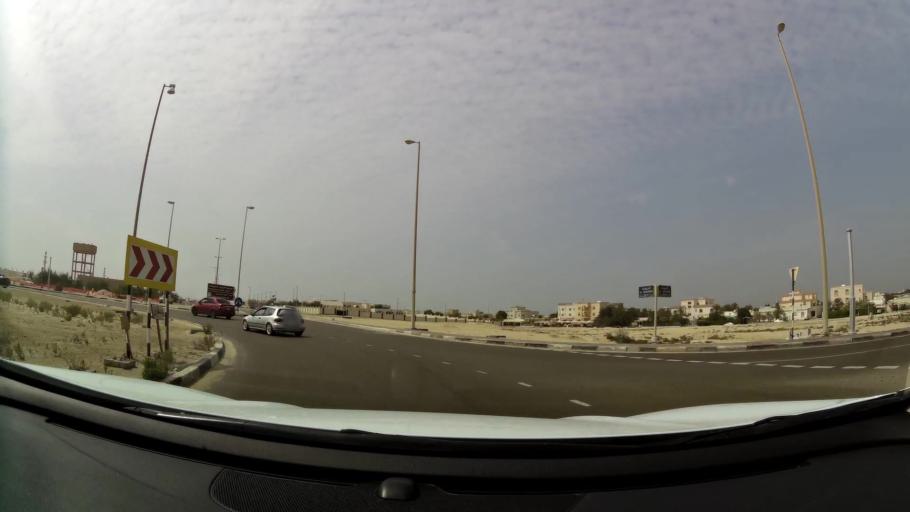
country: AE
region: Abu Dhabi
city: Abu Dhabi
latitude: 24.5419
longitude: 54.6838
